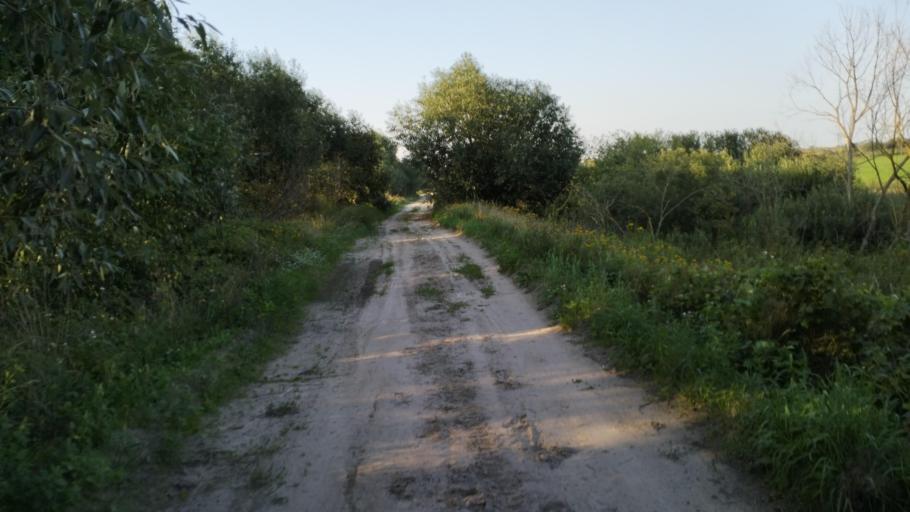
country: BY
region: Brest
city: Davyd-Haradok
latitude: 52.0262
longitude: 27.1944
